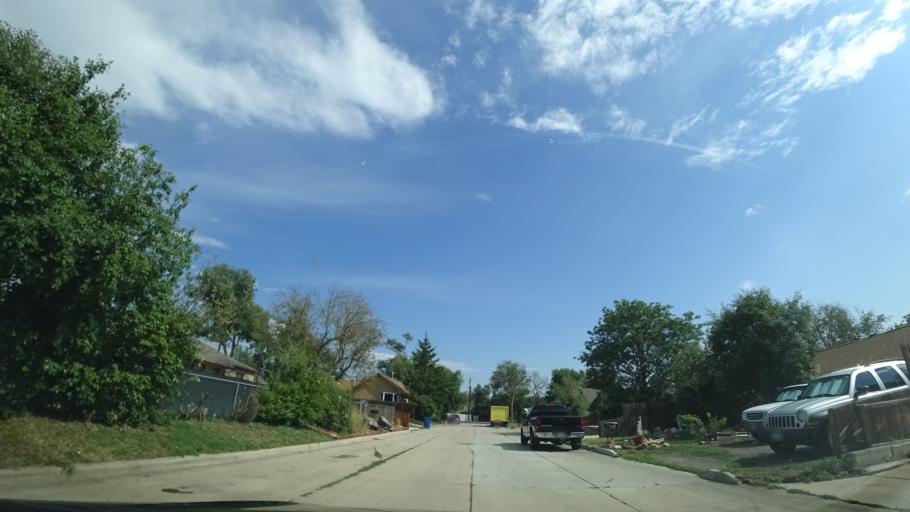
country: US
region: Colorado
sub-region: Jefferson County
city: Lakewood
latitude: 39.7176
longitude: -105.0591
